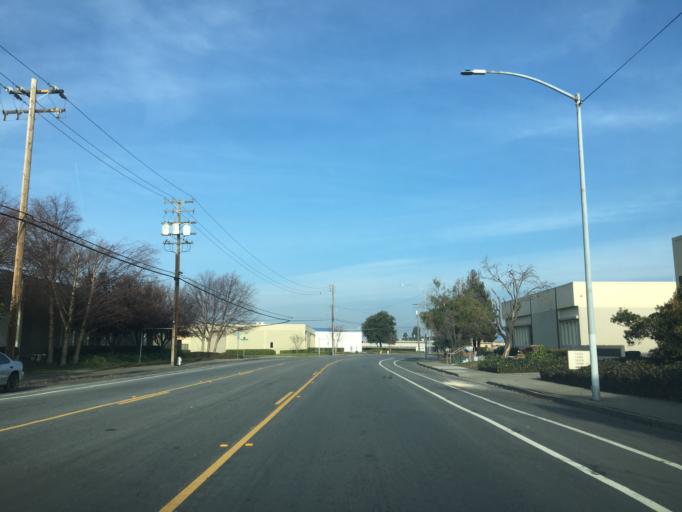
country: US
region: California
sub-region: Alameda County
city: San Leandro
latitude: 37.6978
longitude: -122.1653
